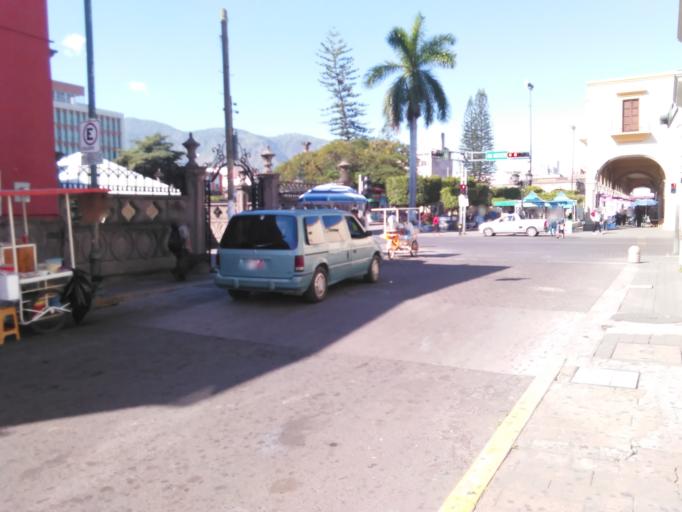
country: MX
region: Nayarit
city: Tepic
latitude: 21.5122
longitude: -104.8913
